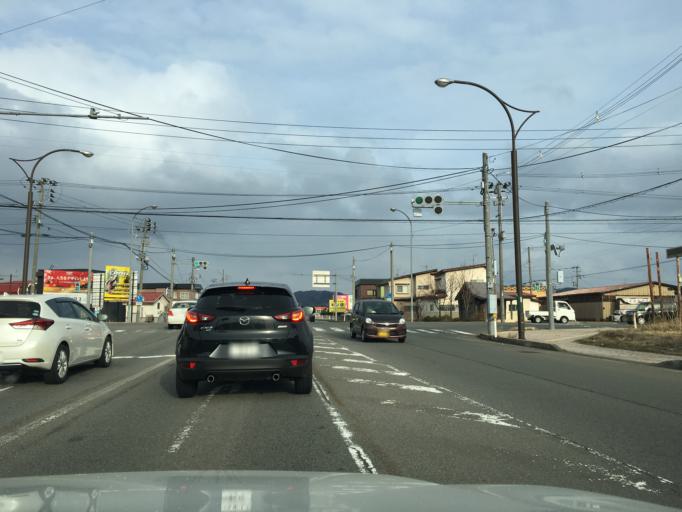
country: JP
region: Aomori
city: Namioka
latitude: 40.7216
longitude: 140.5884
